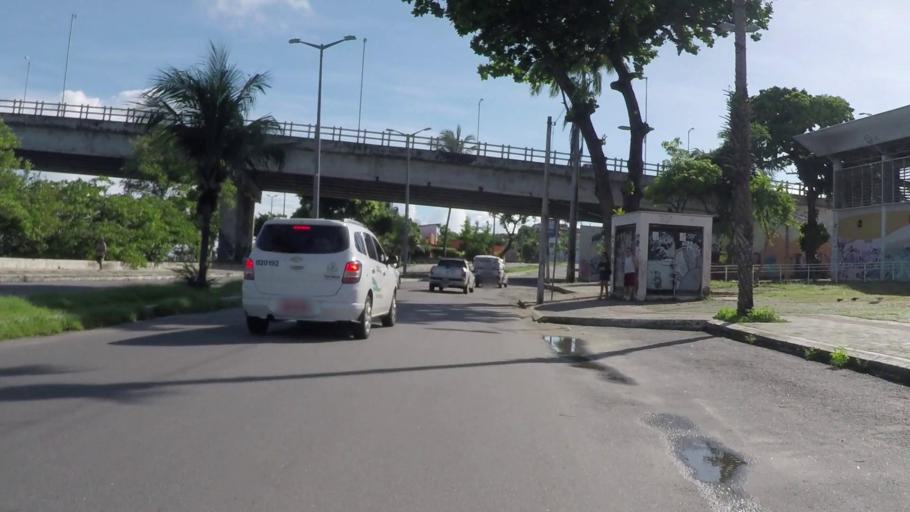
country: BR
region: Ceara
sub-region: Fortaleza
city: Fortaleza
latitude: -3.7003
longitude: -38.5884
